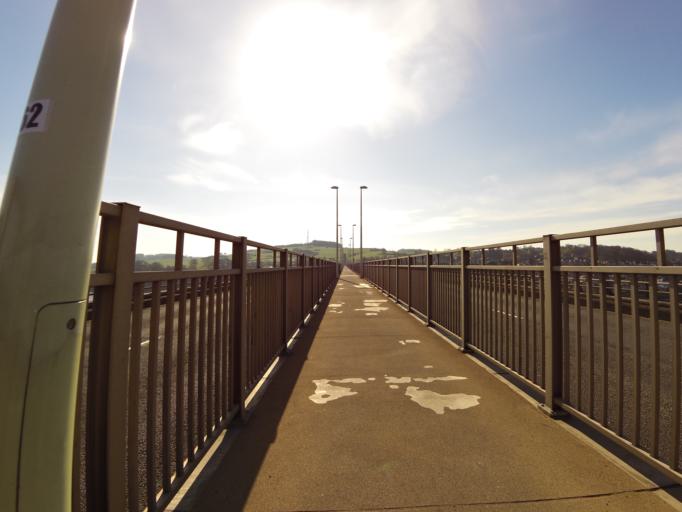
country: GB
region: Scotland
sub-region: Fife
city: Newport-On-Tay
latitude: 56.4493
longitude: -2.9387
